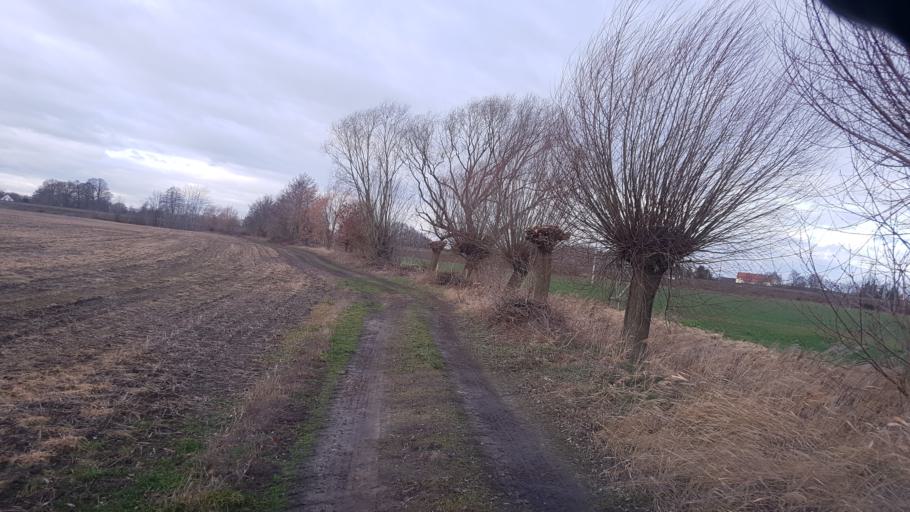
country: DE
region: Brandenburg
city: Doberlug-Kirchhain
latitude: 51.6133
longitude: 13.5670
